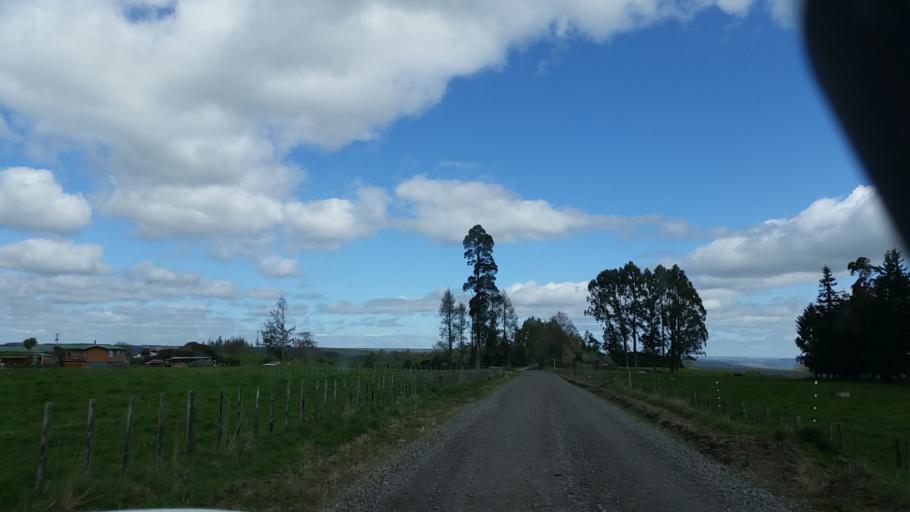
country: NZ
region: Bay of Plenty
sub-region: Whakatane District
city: Murupara
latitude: -38.4780
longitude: 176.4149
